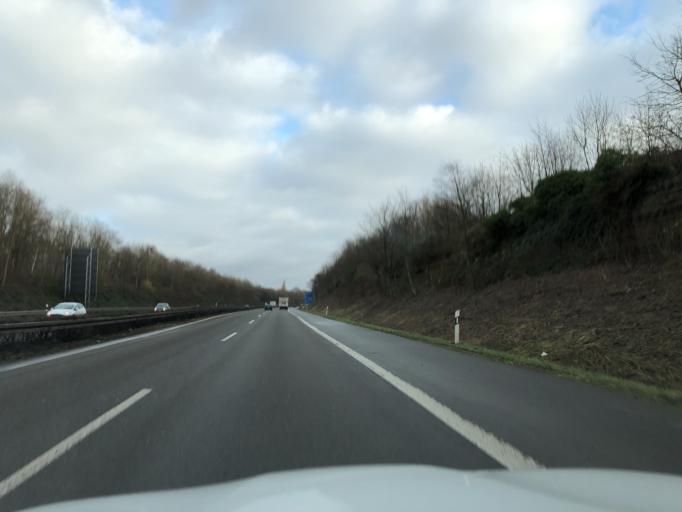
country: DE
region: North Rhine-Westphalia
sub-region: Regierungsbezirk Dusseldorf
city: Hochfeld
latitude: 51.3630
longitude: 6.7678
